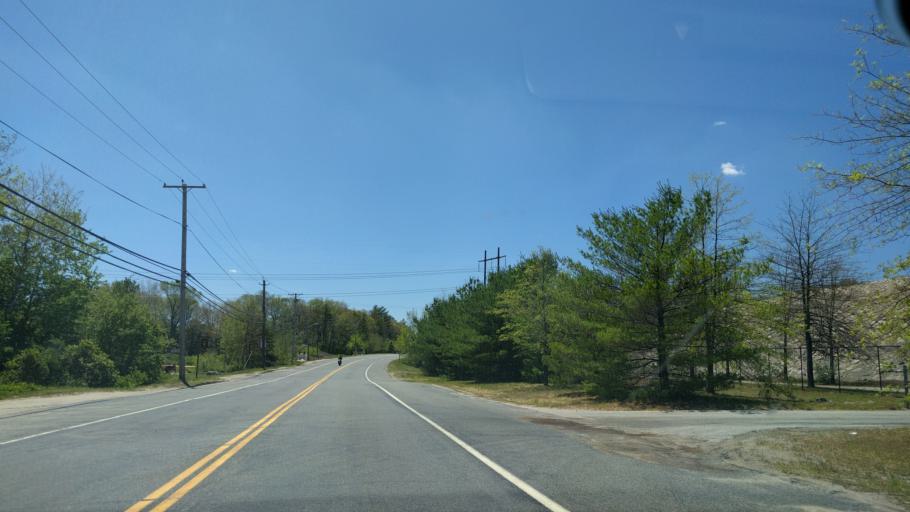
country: US
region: Massachusetts
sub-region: Worcester County
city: Millville
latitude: 41.9881
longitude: -71.6010
